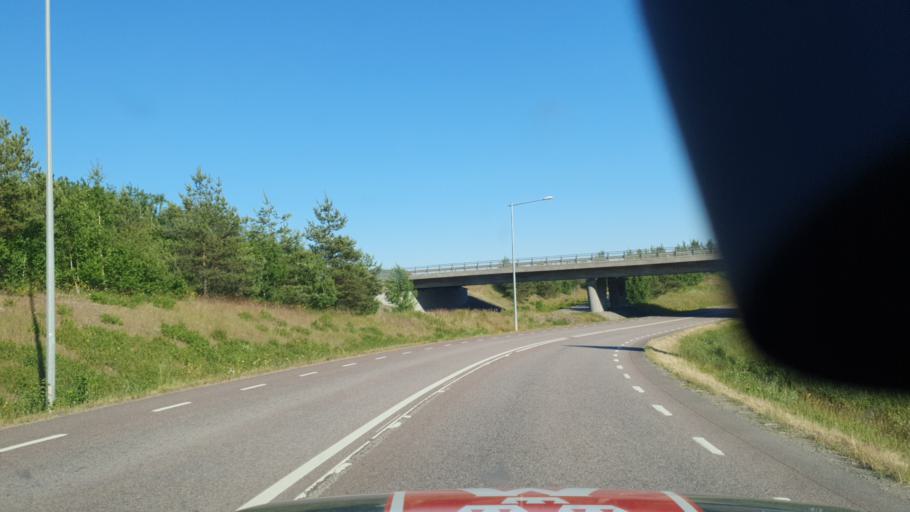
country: SE
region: Kalmar
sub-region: Kalmar Kommun
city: Ljungbyholm
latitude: 56.6236
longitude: 16.1706
